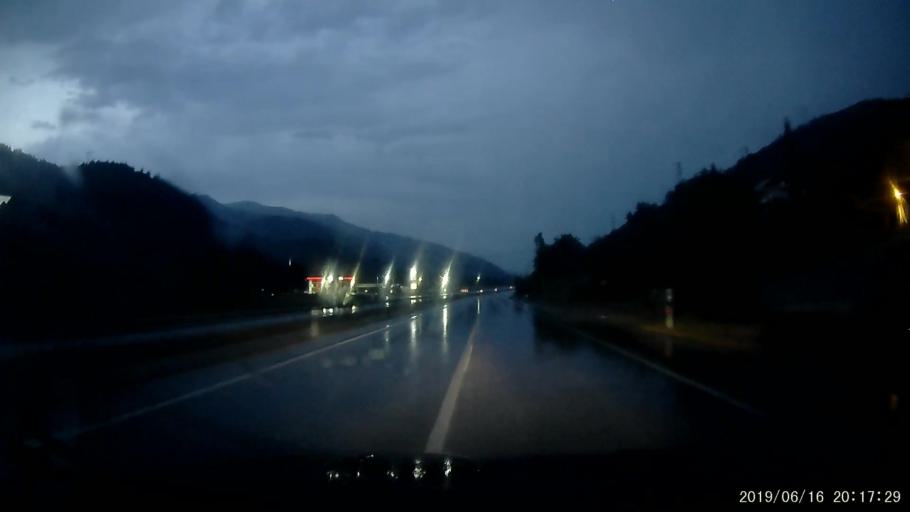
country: TR
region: Tokat
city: Resadiye
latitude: 40.3653
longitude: 37.4216
